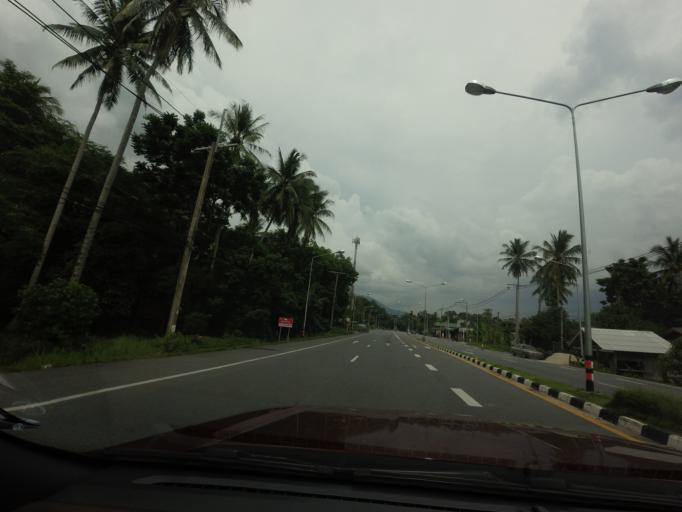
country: TH
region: Yala
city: Krong Pi Nang
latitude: 6.4677
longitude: 101.2703
